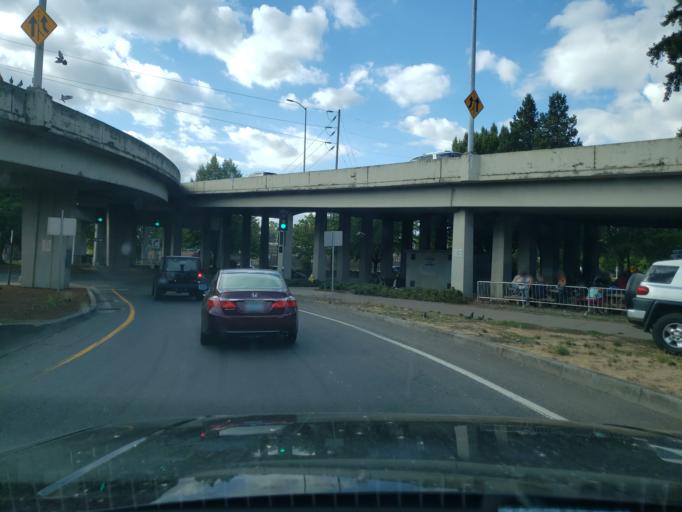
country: US
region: Oregon
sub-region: Marion County
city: Salem
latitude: 44.9449
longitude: -123.0395
